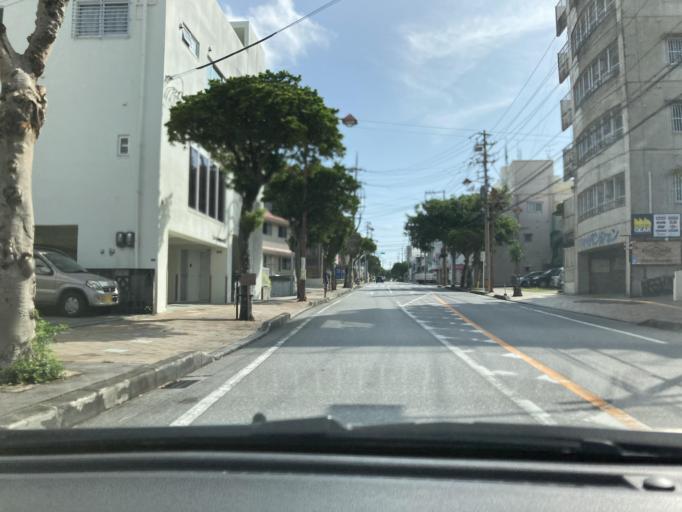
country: JP
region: Okinawa
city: Chatan
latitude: 26.2895
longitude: 127.7798
